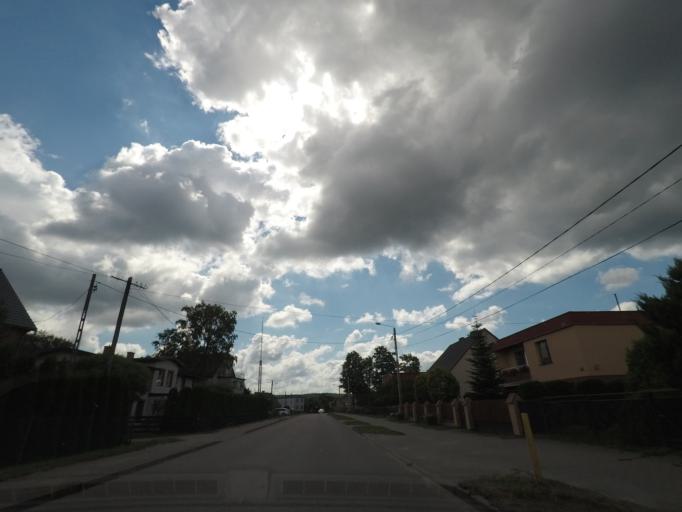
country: PL
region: Pomeranian Voivodeship
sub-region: Powiat wejherowski
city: Leczyce
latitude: 54.5854
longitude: 17.8628
